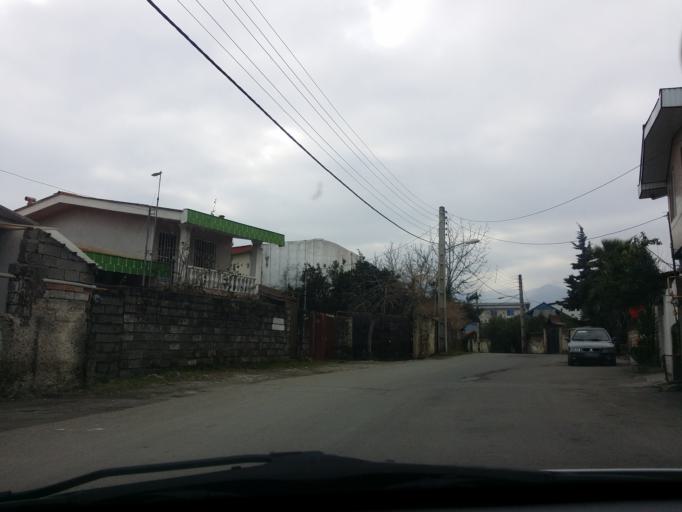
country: IR
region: Mazandaran
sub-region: Nowshahr
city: Nowshahr
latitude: 36.6569
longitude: 51.4771
